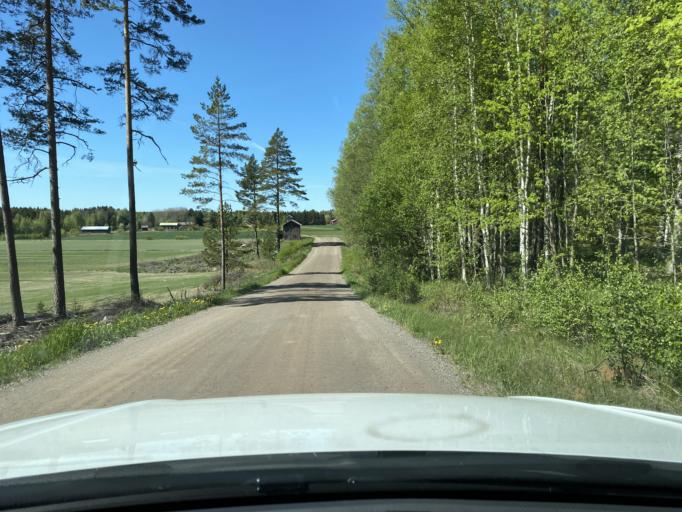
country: FI
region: Satakunta
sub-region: Rauma
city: Lappi
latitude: 61.1367
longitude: 21.9675
